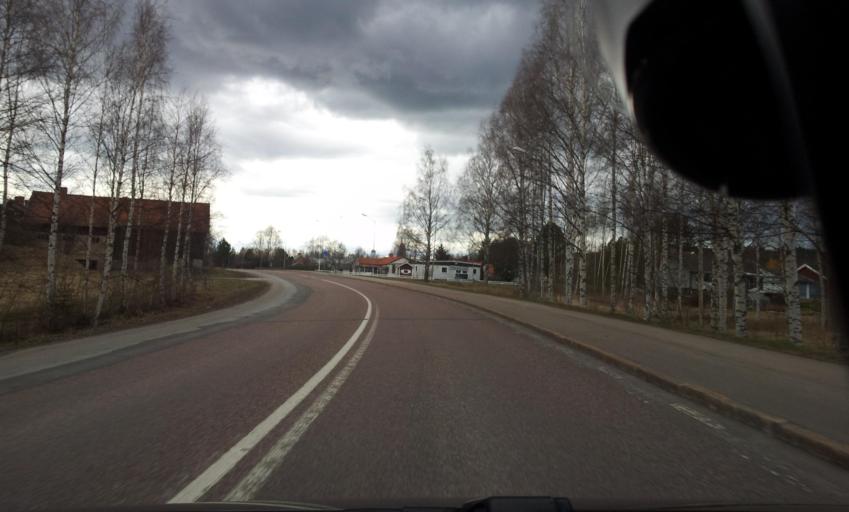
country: SE
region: Gaevleborg
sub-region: Ljusdals Kommun
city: Ljusdal
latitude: 61.8345
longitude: 16.0673
